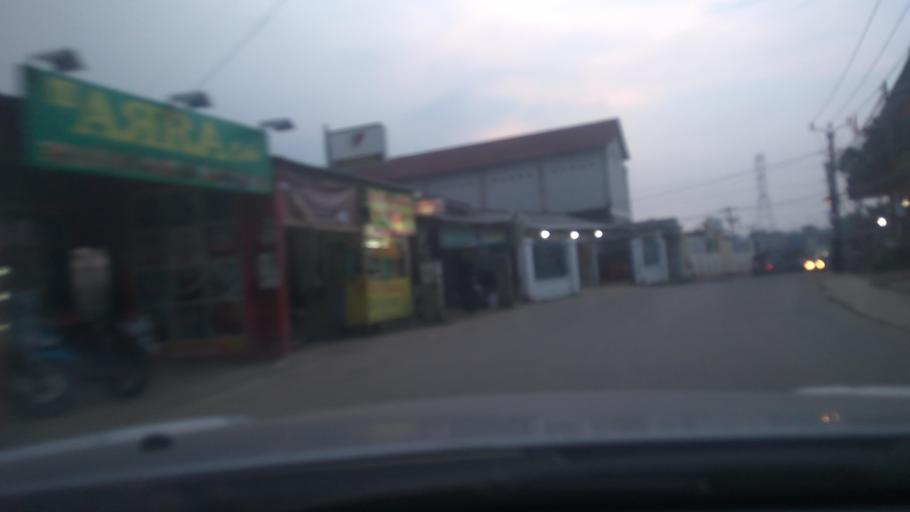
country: ID
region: West Java
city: Pamulang
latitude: -6.3696
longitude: 106.7389
